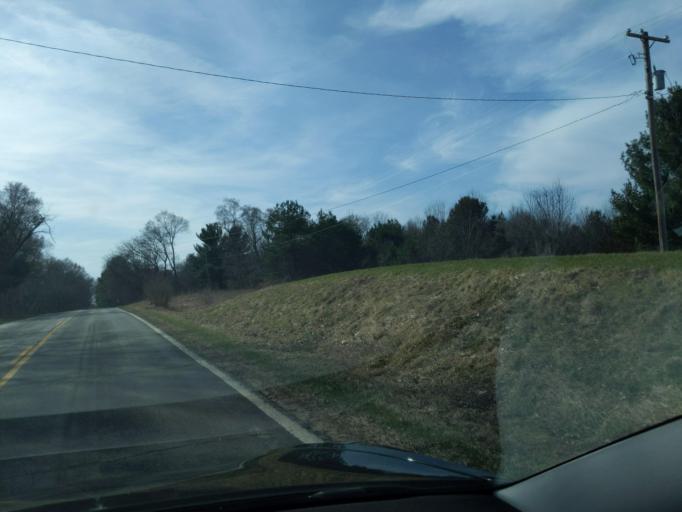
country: US
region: Michigan
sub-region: Ingham County
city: Stockbridge
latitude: 42.4899
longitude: -84.3013
